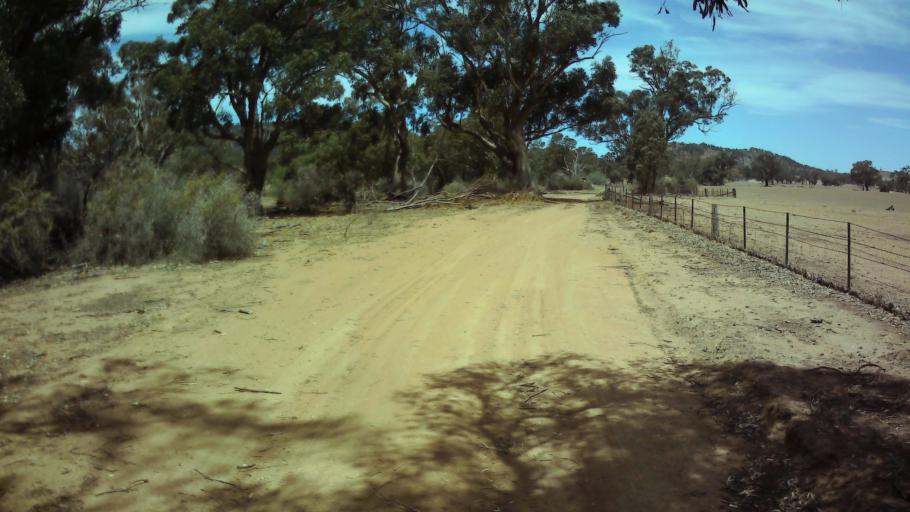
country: AU
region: New South Wales
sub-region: Weddin
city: Grenfell
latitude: -33.7645
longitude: 148.1479
